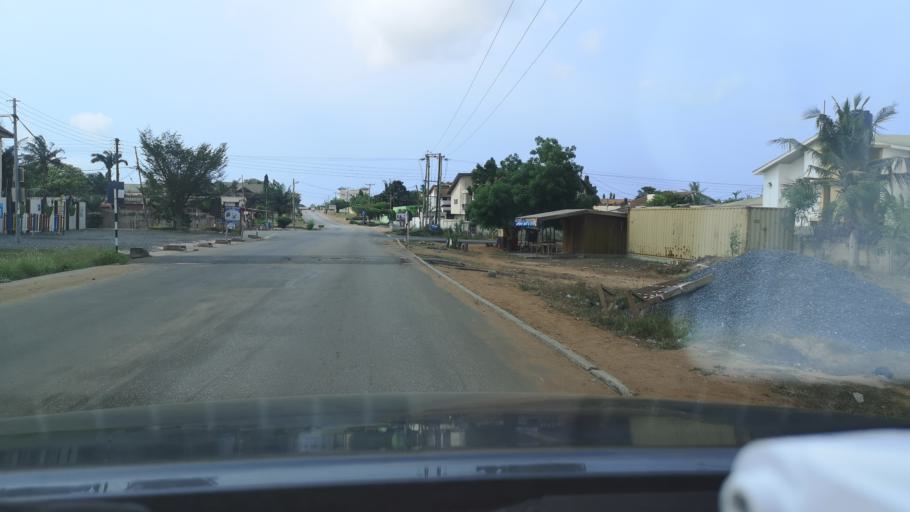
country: GH
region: Greater Accra
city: Tema
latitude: 5.6756
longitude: -0.0300
